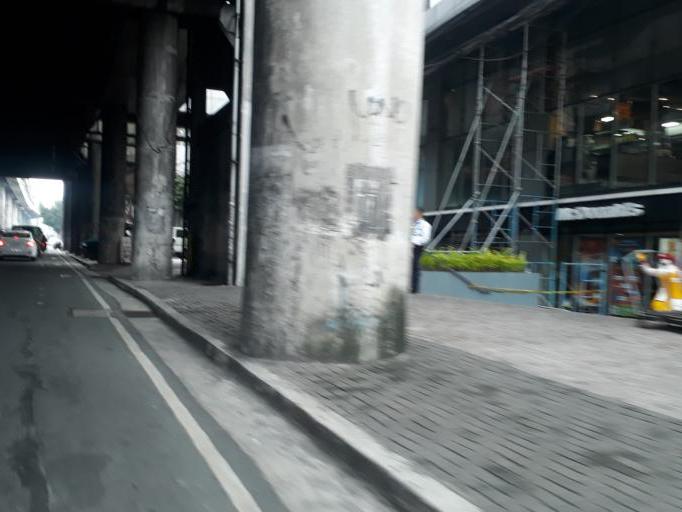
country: PH
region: Metro Manila
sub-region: Quezon City
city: Quezon City
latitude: 14.6278
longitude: 121.0643
